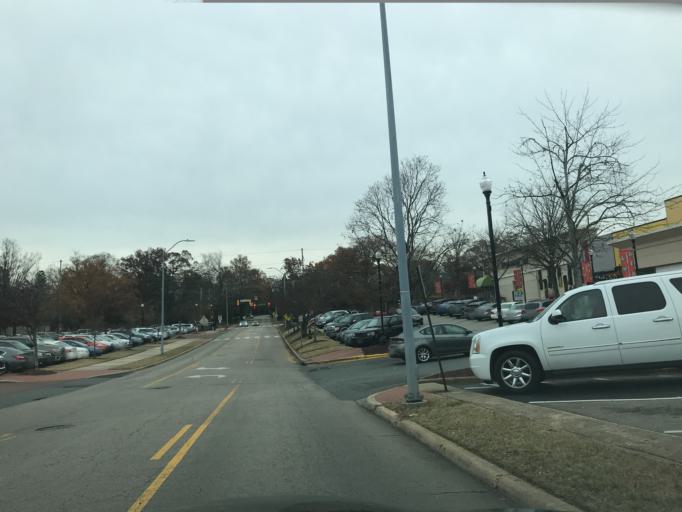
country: US
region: North Carolina
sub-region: Wake County
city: West Raleigh
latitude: 35.7902
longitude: -78.6593
